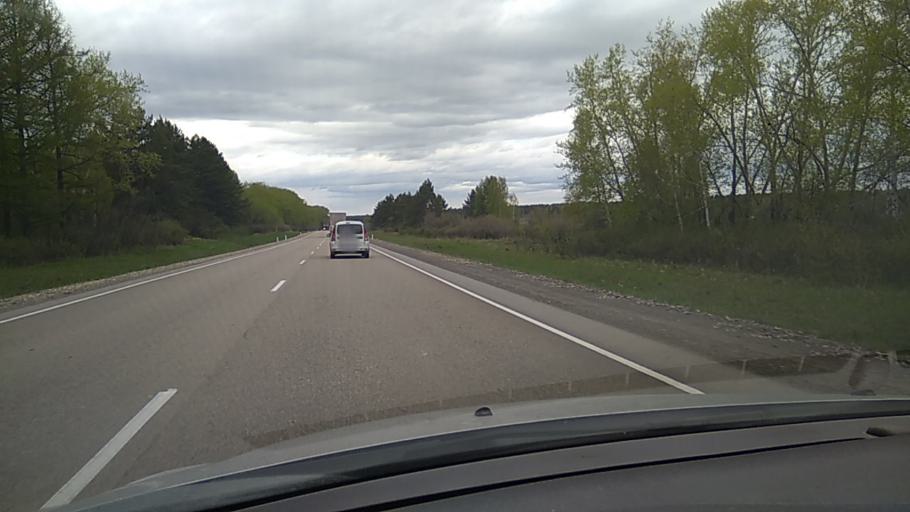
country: RU
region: Sverdlovsk
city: Dvurechensk
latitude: 56.6688
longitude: 61.1518
